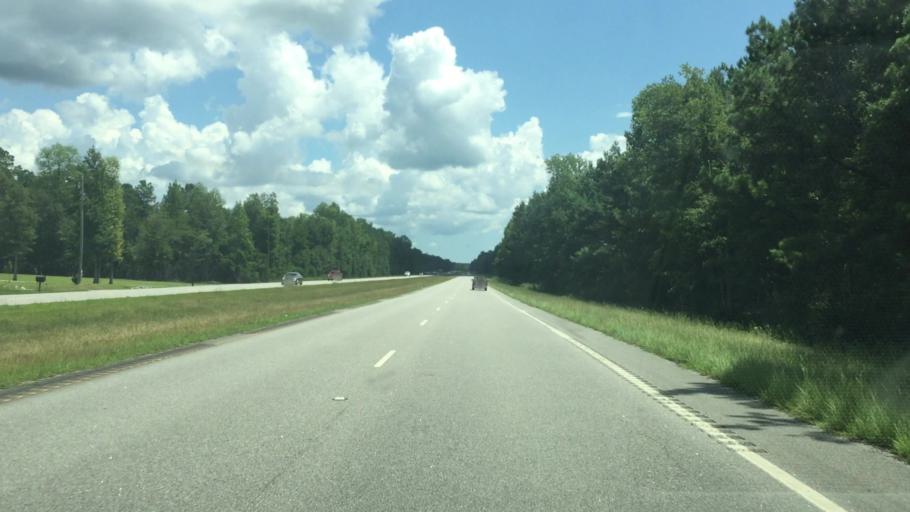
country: US
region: South Carolina
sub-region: Horry County
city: Loris
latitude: 34.0449
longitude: -78.8293
